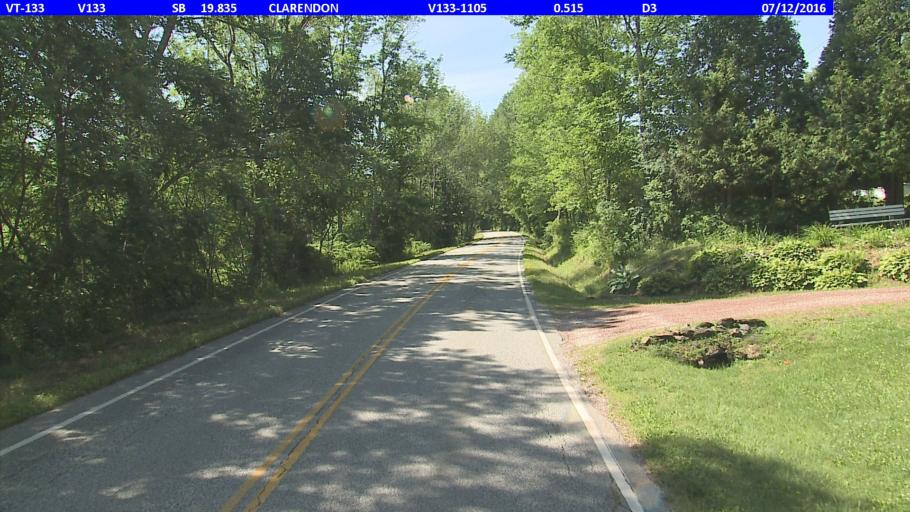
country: US
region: Vermont
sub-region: Rutland County
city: West Rutland
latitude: 43.5582
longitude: -73.0359
